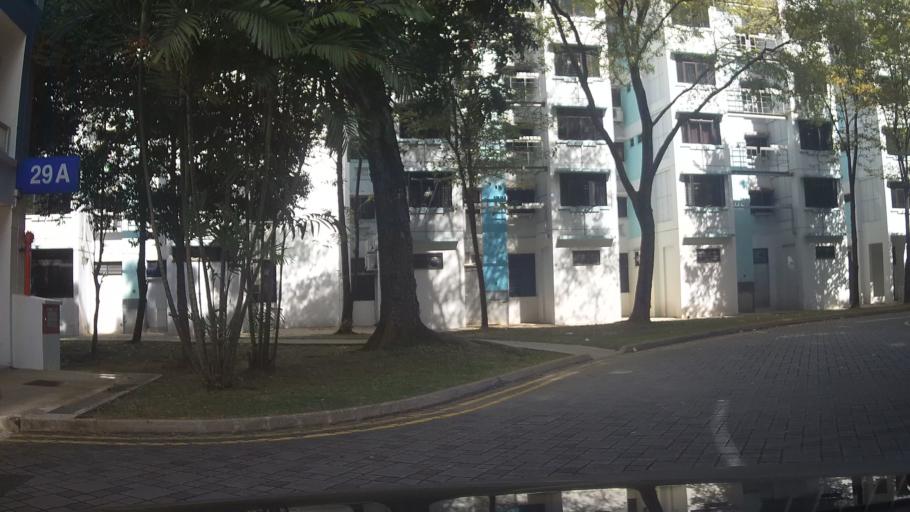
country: MY
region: Johor
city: Johor Bahru
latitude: 1.4428
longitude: 103.7733
